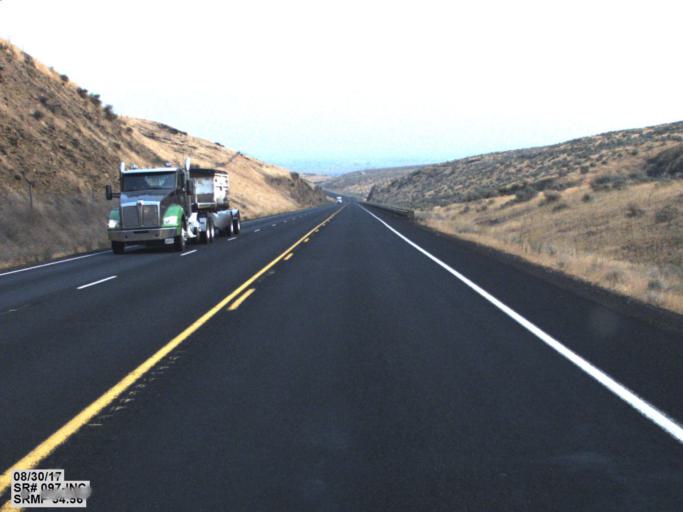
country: US
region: Washington
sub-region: Yakima County
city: Toppenish
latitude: 46.2844
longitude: -120.3644
